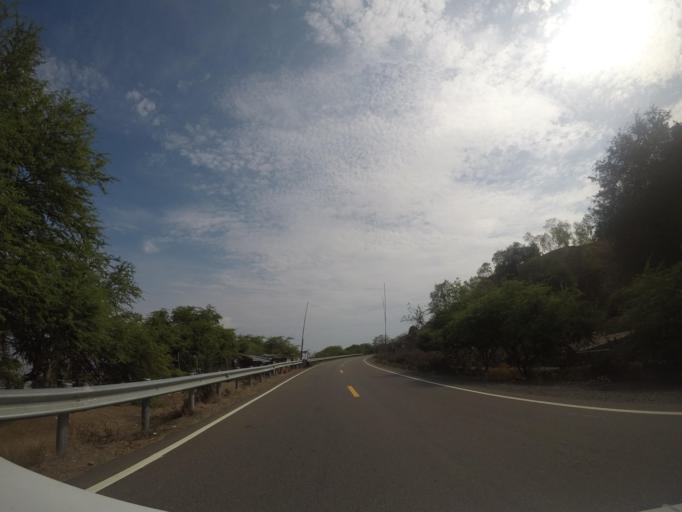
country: ID
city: Metinaro
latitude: -8.5269
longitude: 125.7099
